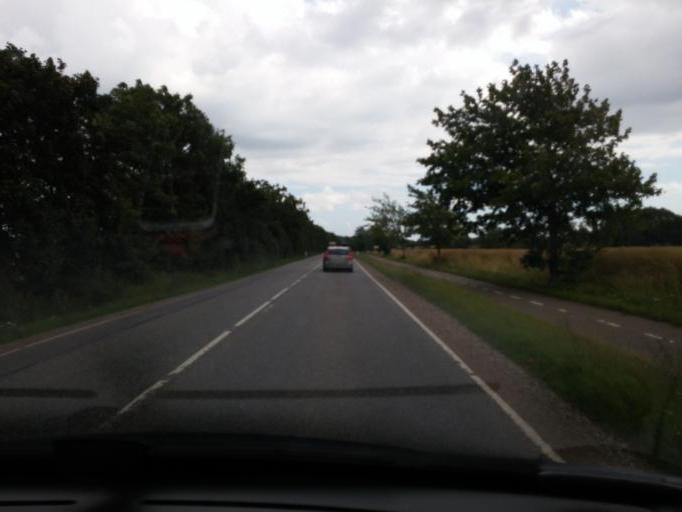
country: DK
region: South Denmark
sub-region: Svendborg Kommune
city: Vindeby
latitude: 54.9933
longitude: 10.6166
